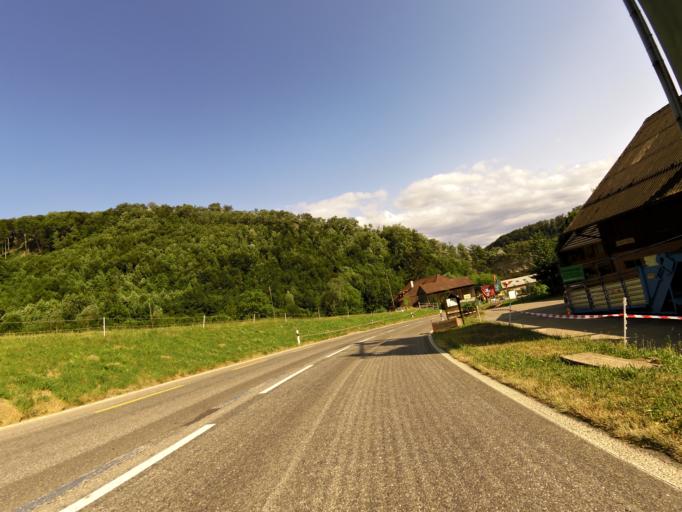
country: CH
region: Solothurn
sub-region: Bezirk Goesgen
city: Trimbach
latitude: 47.3694
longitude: 7.8825
